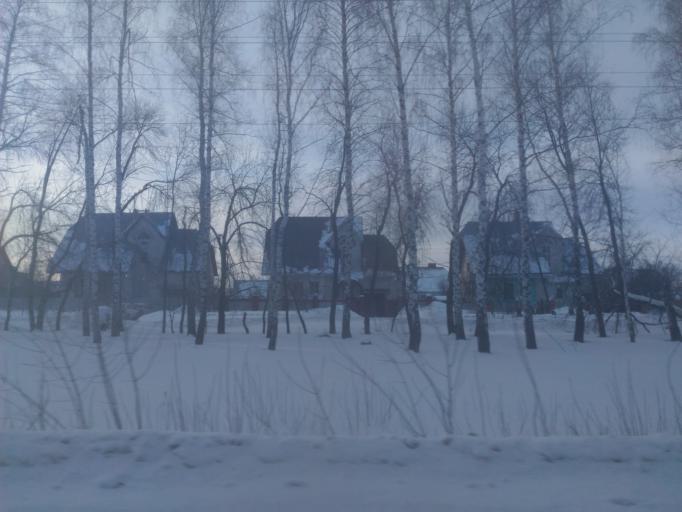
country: RU
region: Ulyanovsk
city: Isheyevka
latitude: 54.4301
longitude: 48.2901
